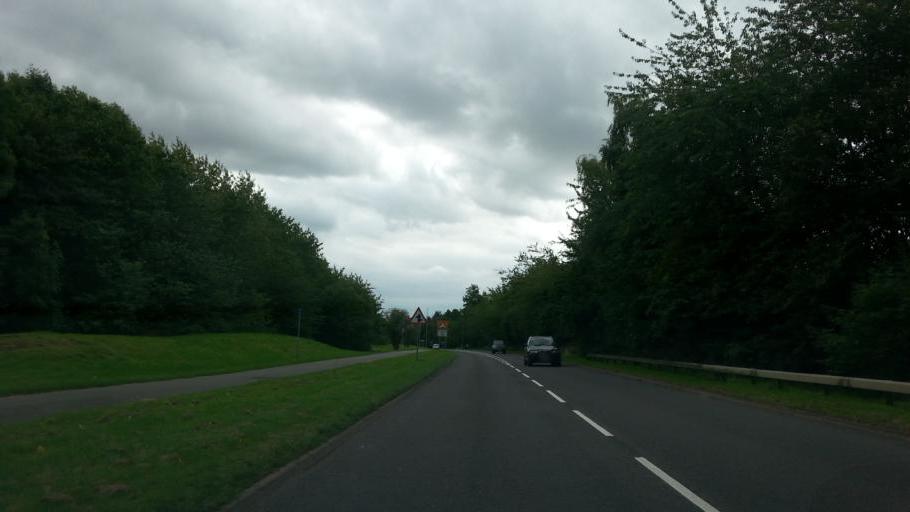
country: GB
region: England
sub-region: Northamptonshire
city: Earls Barton
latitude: 52.2680
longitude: -0.8123
